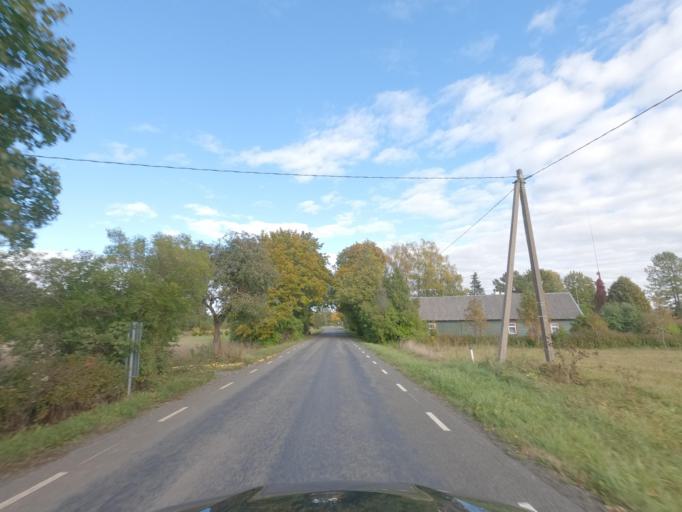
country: EE
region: Raplamaa
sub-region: Maerjamaa vald
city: Marjamaa
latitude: 58.8231
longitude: 24.6201
